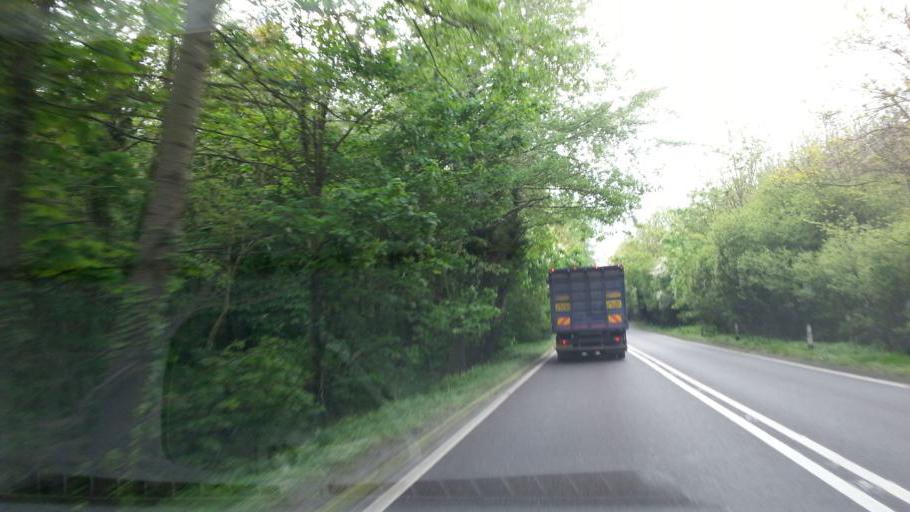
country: GB
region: England
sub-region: Nottinghamshire
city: South Collingham
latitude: 53.0797
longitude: -0.7116
